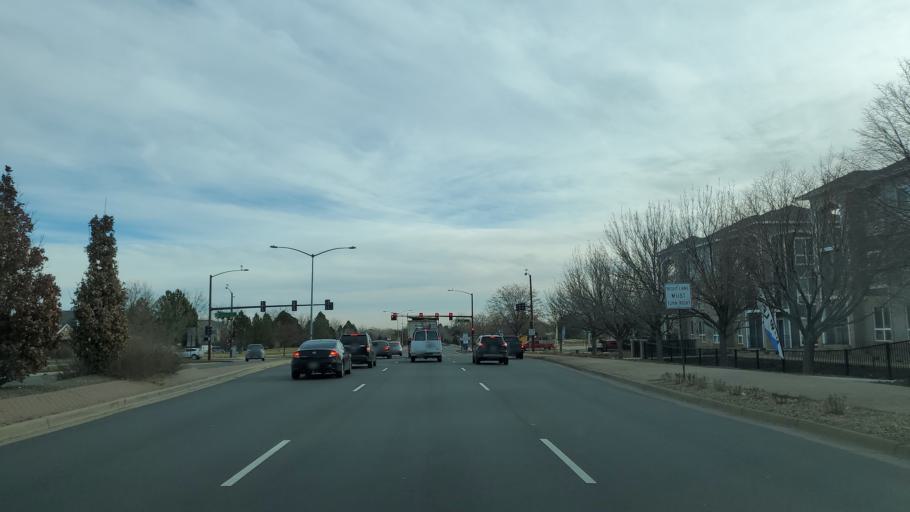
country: US
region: Colorado
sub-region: Adams County
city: Northglenn
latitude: 39.9138
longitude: -104.9545
